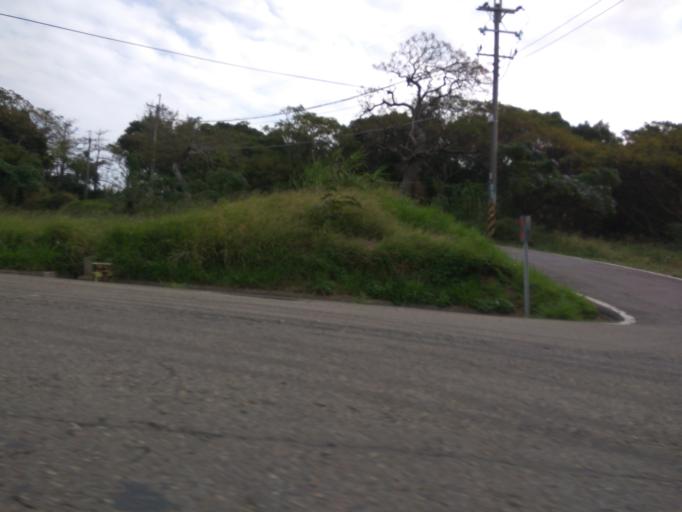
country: TW
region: Taiwan
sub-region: Hsinchu
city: Zhubei
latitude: 24.9567
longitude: 121.0125
